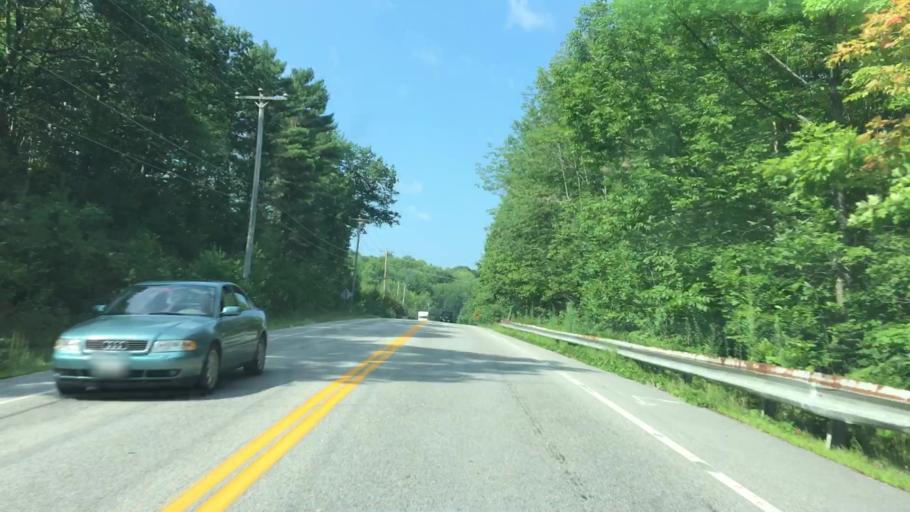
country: US
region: Maine
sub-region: Androscoggin County
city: Minot
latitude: 44.0281
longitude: -70.3125
